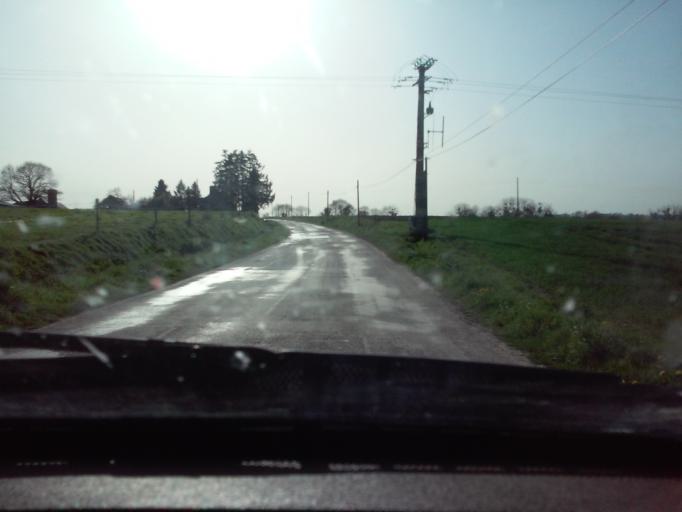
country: FR
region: Brittany
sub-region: Departement d'Ille-et-Vilaine
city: Romagne
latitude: 48.3097
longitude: -1.2544
